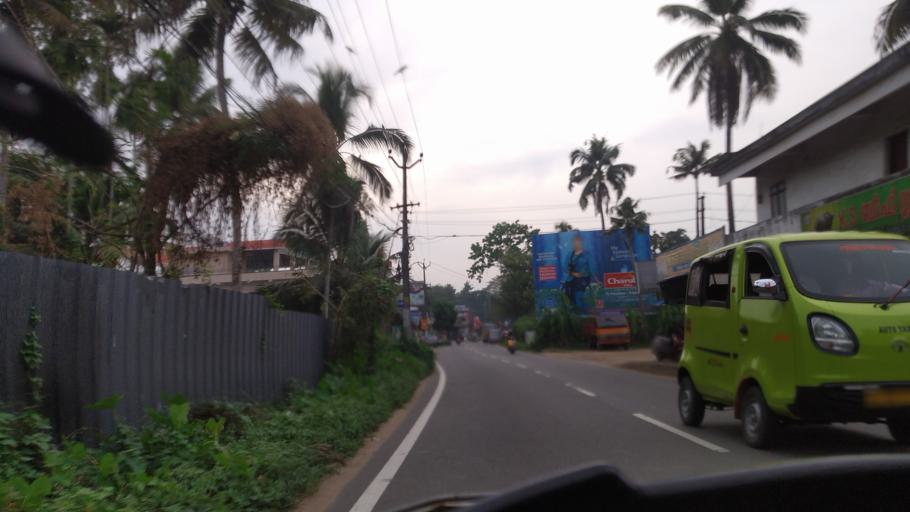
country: IN
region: Kerala
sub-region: Thrissur District
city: Kodungallur
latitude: 10.1484
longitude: 76.2471
